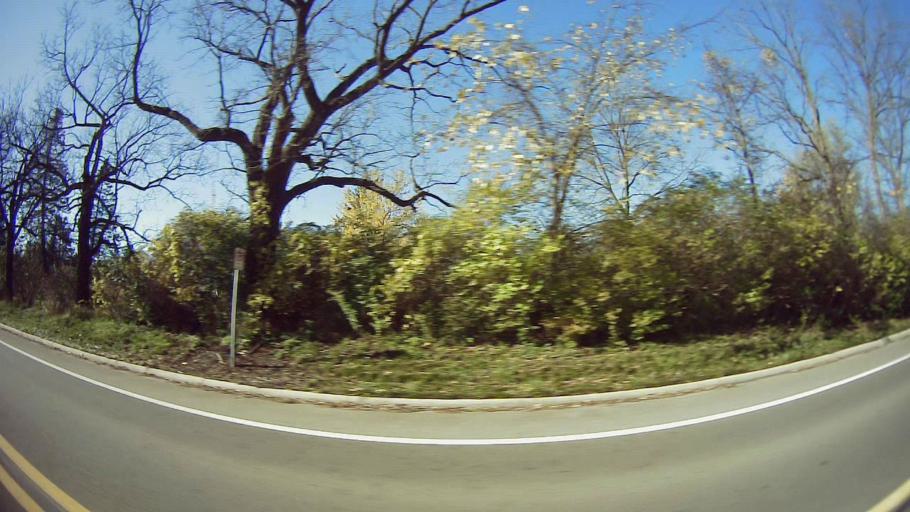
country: US
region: Michigan
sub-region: Oakland County
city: Farmington Hills
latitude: 42.4757
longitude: -83.3770
